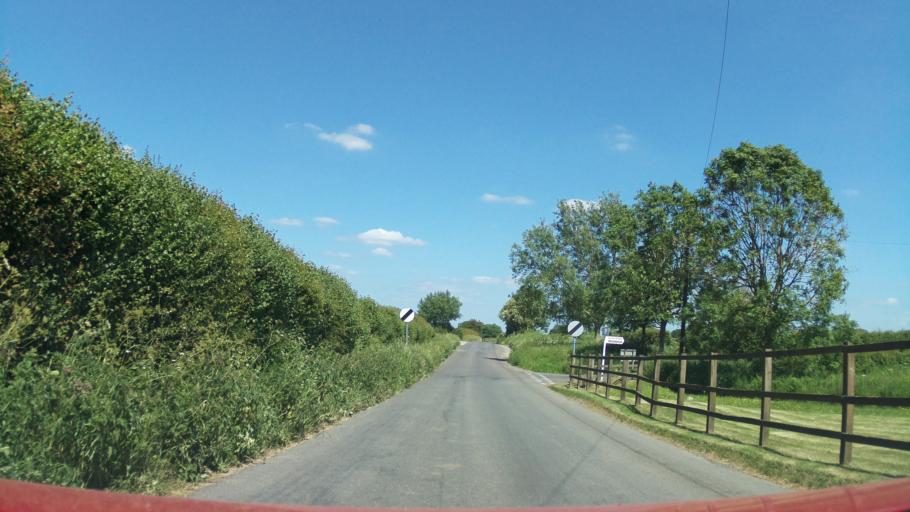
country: GB
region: England
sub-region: Wiltshire
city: Royal Wootton Bassett
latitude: 51.5044
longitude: -1.9080
